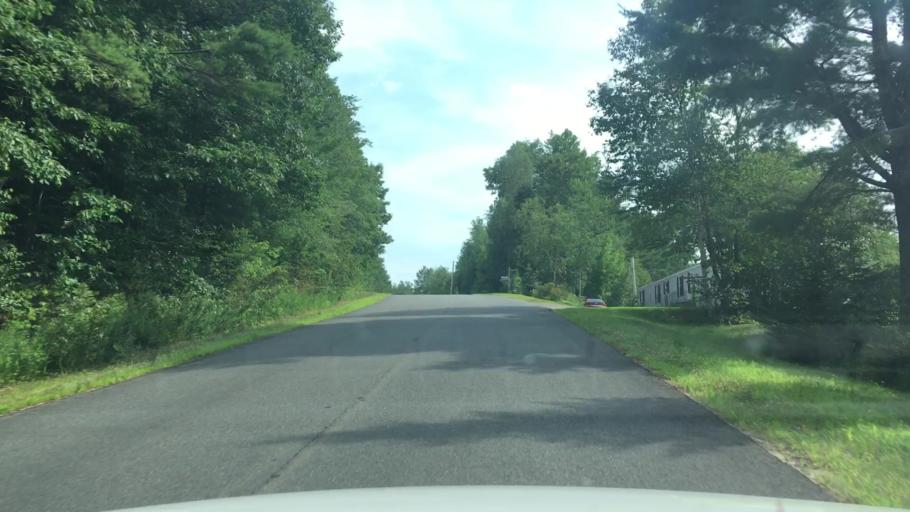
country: US
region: Maine
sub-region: Lincoln County
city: Jefferson
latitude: 44.2429
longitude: -69.4458
